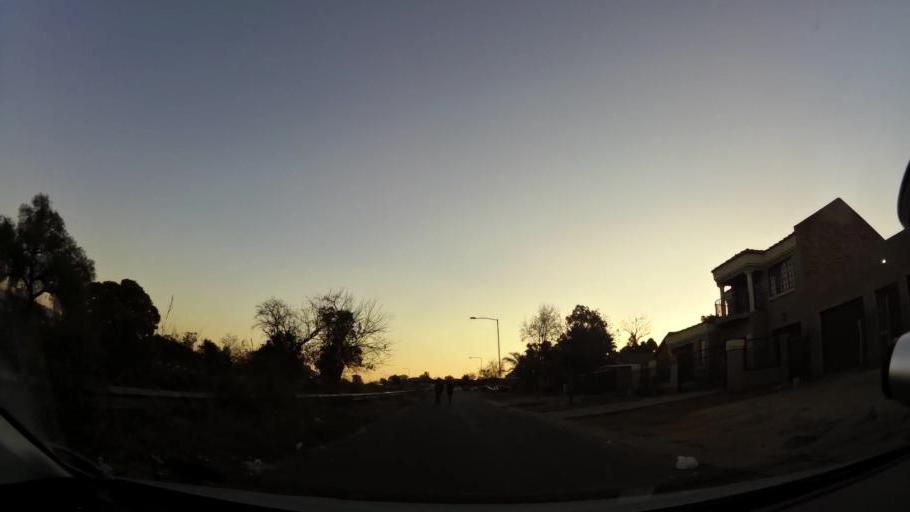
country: ZA
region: Gauteng
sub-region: City of Tshwane Metropolitan Municipality
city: Pretoria
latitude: -25.7425
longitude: 28.1515
